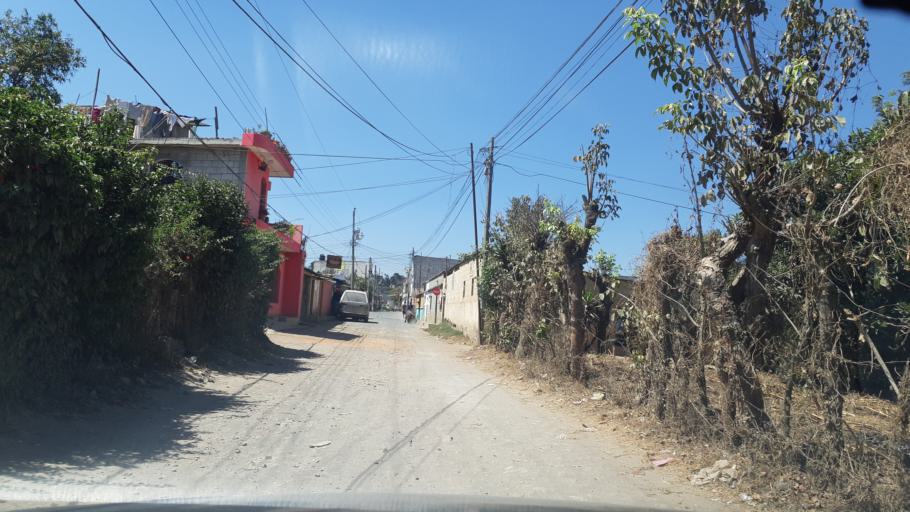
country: GT
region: Chimaltenango
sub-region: Municipio de Chimaltenango
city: Chimaltenango
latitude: 14.6505
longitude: -90.8110
